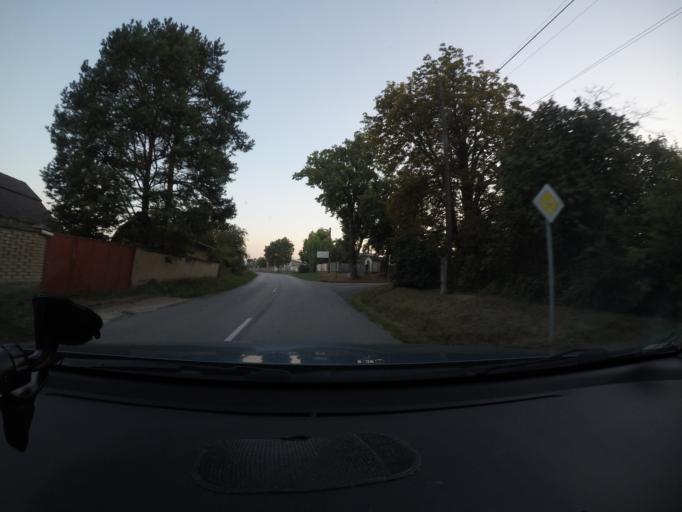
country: SK
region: Trenciansky
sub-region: Okres Nove Mesto nad Vahom
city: Nove Mesto nad Vahom
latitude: 48.8386
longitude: 17.9096
